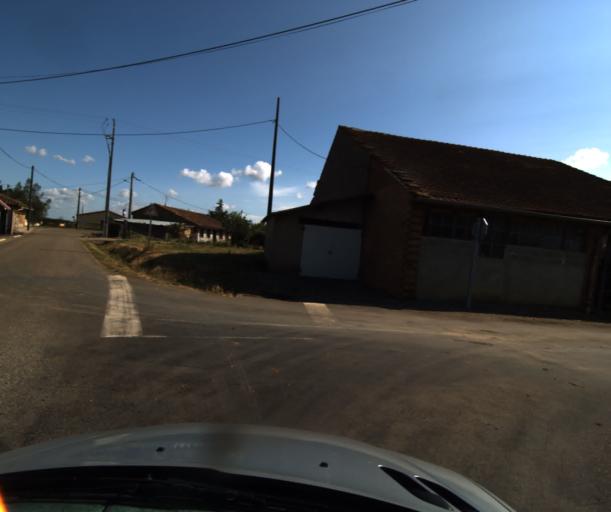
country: FR
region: Midi-Pyrenees
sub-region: Departement du Tarn-et-Garonne
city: Finhan
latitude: 43.9161
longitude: 1.2669
